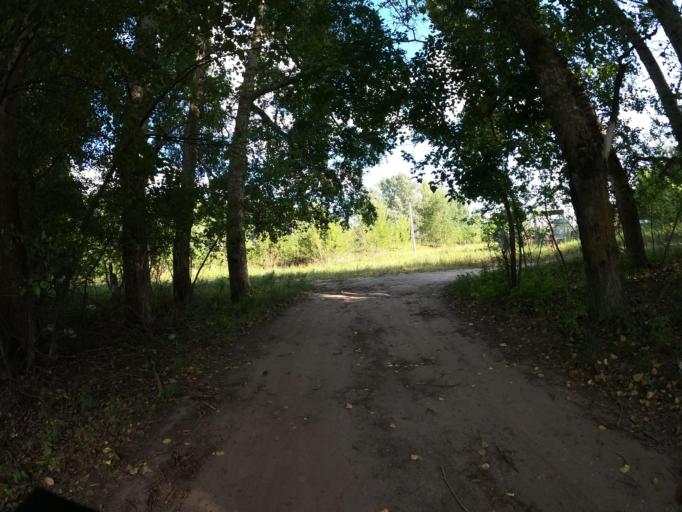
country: RU
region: Moskovskaya
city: Peski
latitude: 55.1925
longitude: 38.7473
